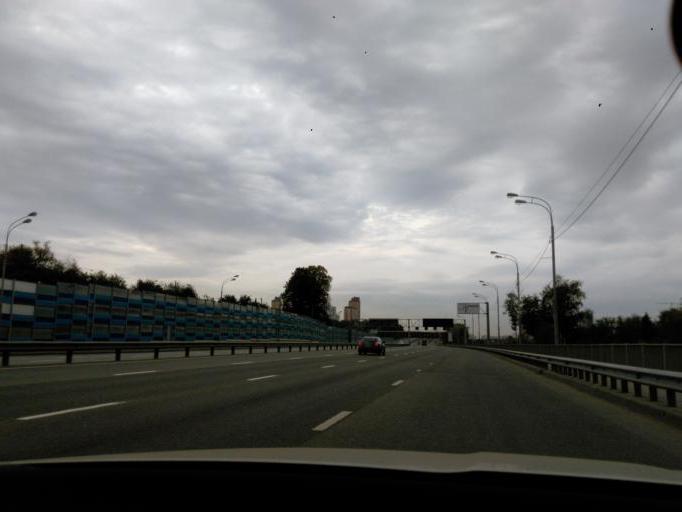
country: RU
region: Moscow
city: Severnyy
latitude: 55.9411
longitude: 37.5438
